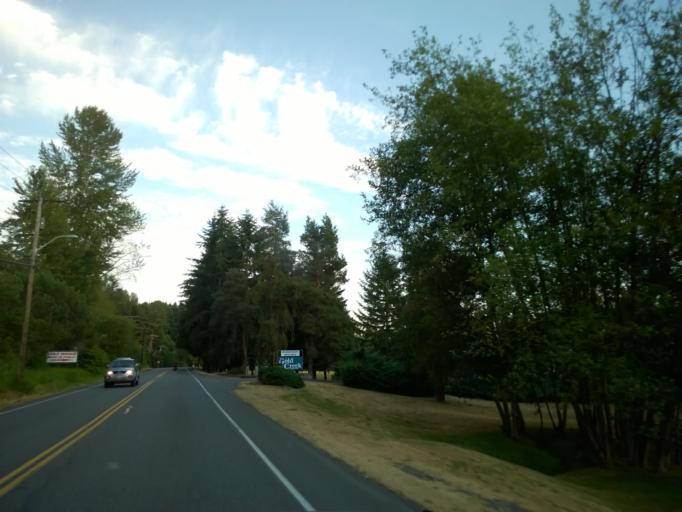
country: US
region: Washington
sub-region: King County
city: Woodinville
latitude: 47.7407
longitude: -122.1440
